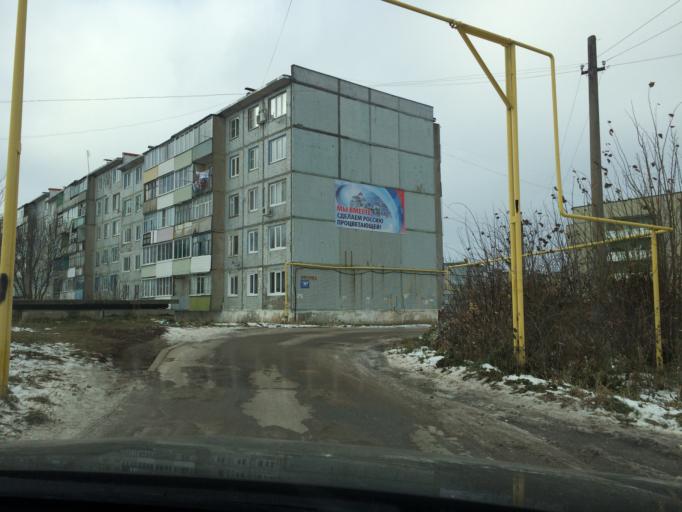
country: RU
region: Tula
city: Plavsk
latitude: 53.7030
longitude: 37.2780
